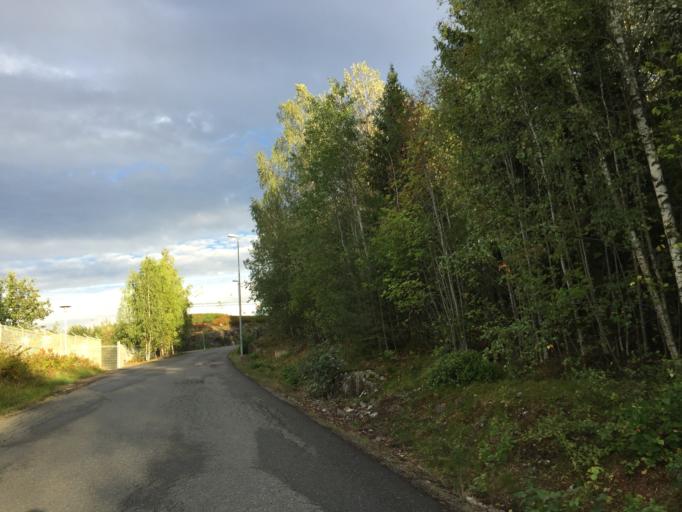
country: NO
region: Akershus
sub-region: Oppegard
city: Kolbotn
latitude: 59.8423
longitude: 10.8168
